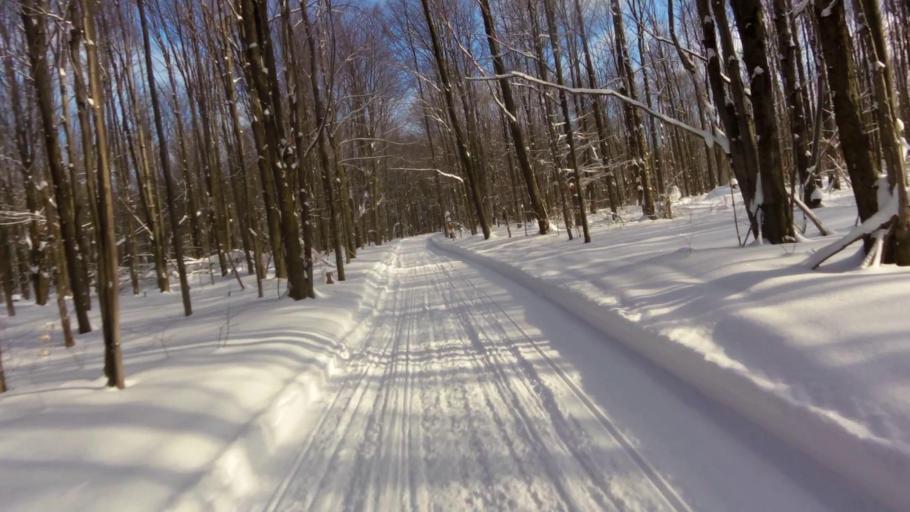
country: US
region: New York
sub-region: Chautauqua County
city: Falconer
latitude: 42.2721
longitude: -79.1396
